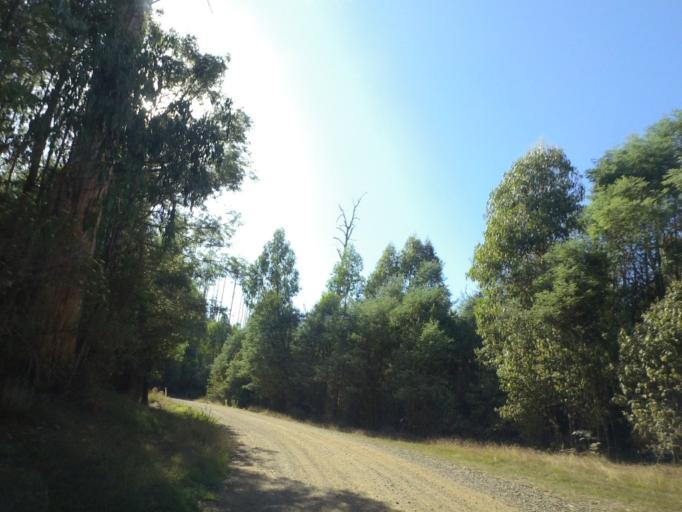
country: AU
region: Victoria
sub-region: Yarra Ranges
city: Millgrove
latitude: -37.5051
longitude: 145.7758
